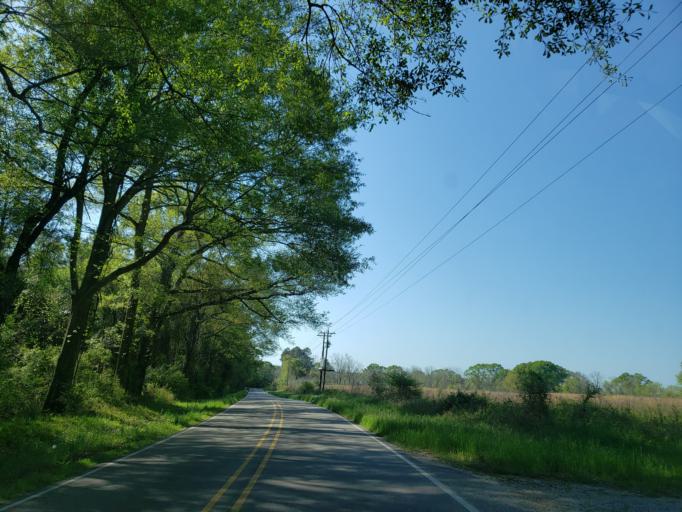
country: US
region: Mississippi
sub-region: Jones County
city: Ellisville
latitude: 31.5797
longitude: -89.3744
